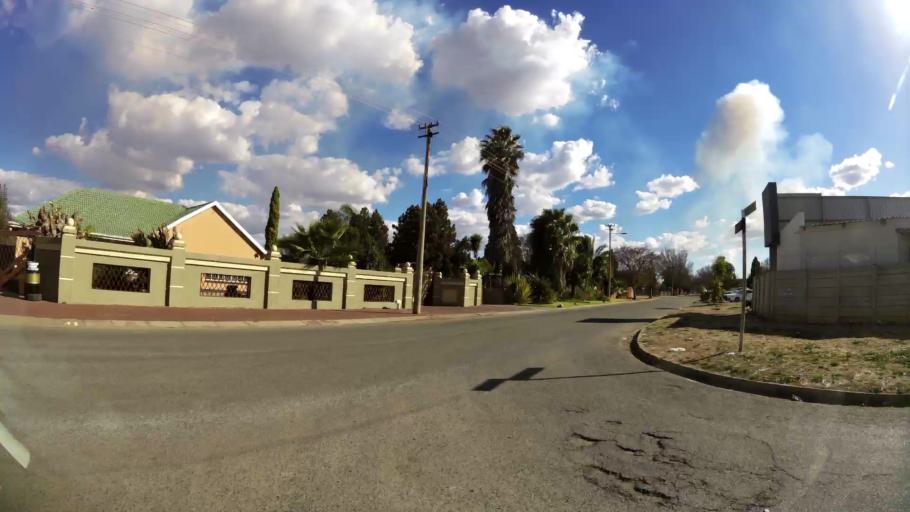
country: ZA
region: North-West
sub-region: Dr Kenneth Kaunda District Municipality
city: Klerksdorp
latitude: -26.8266
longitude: 26.6582
